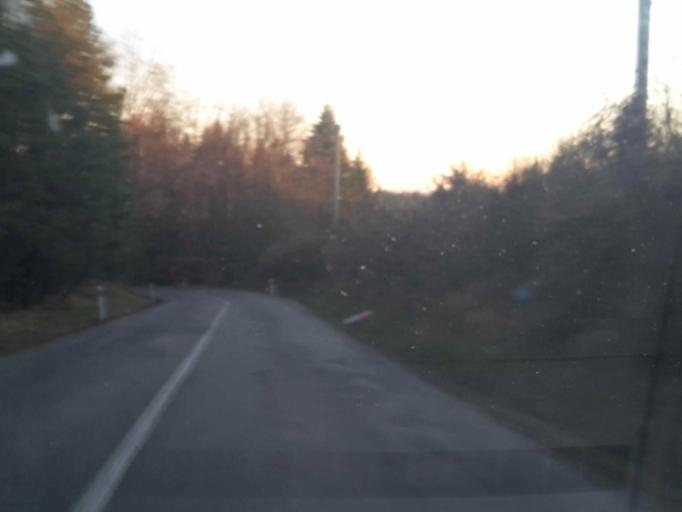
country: CZ
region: South Moravian
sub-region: Okres Blansko
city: Adamov
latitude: 49.2800
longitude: 16.6327
